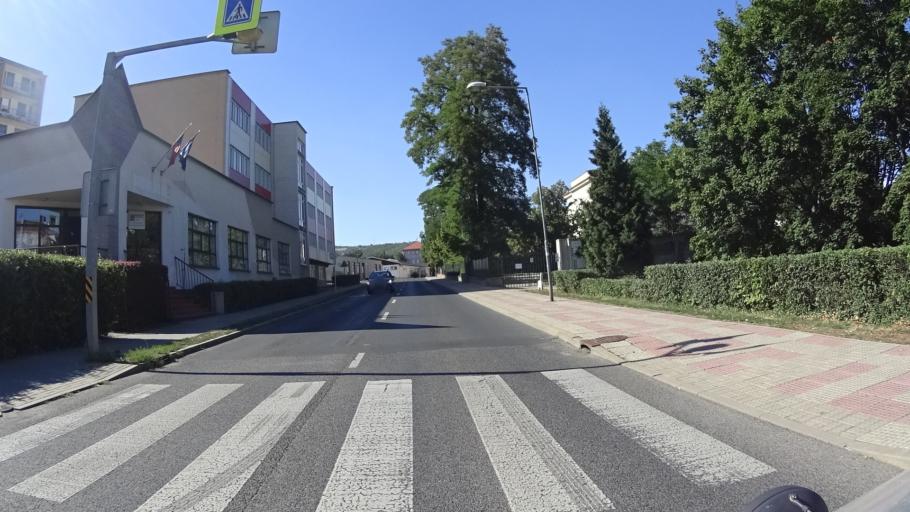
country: CZ
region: Ustecky
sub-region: Okres Litomerice
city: Litomerice
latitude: 50.5388
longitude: 14.1271
